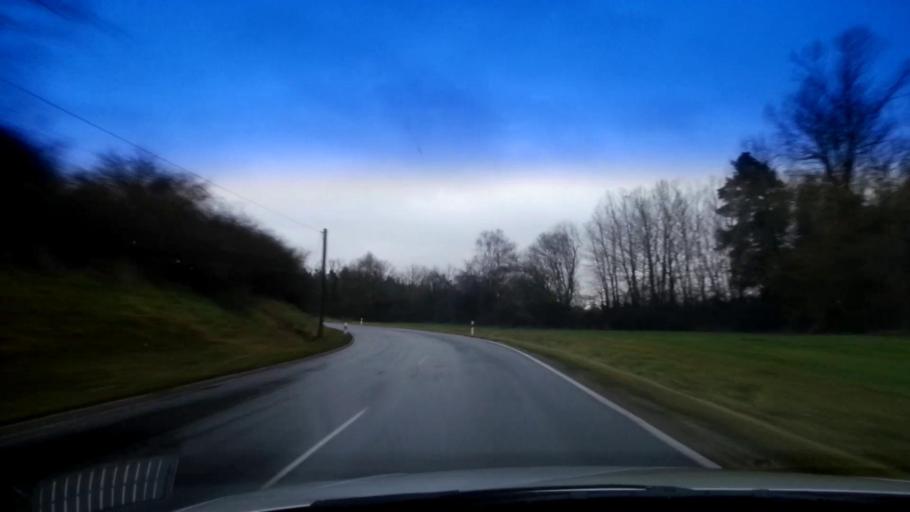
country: DE
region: Bavaria
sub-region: Upper Franconia
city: Lauter
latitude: 49.9644
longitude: 10.8040
